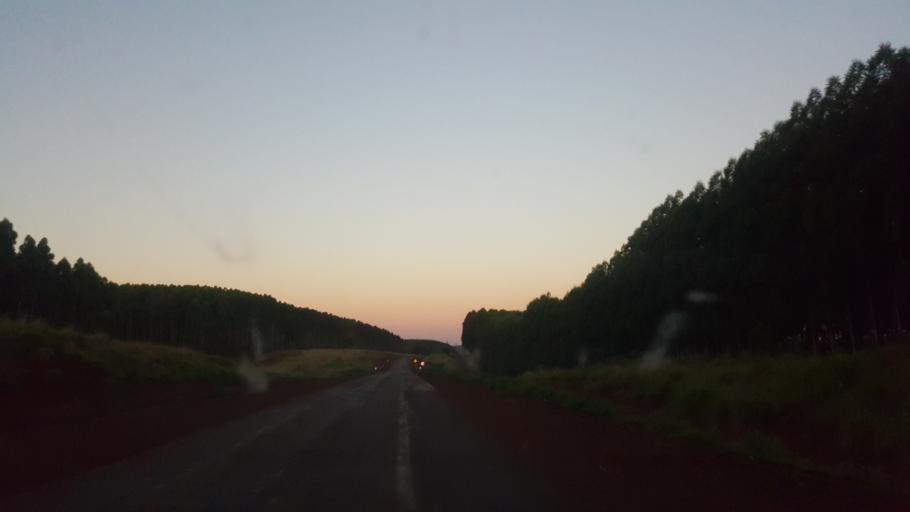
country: AR
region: Corrientes
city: Garruchos
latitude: -28.2501
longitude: -55.8459
